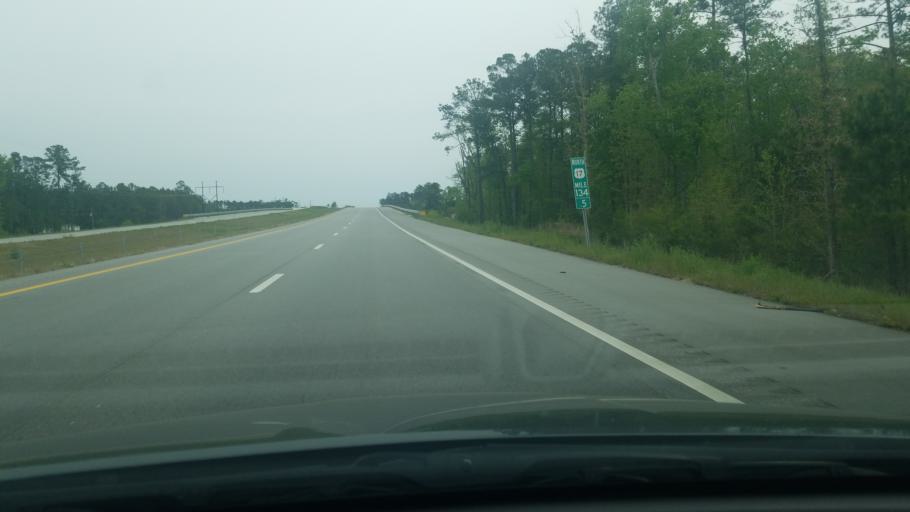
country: US
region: North Carolina
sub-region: Craven County
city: River Bend
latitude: 35.0499
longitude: -77.2149
